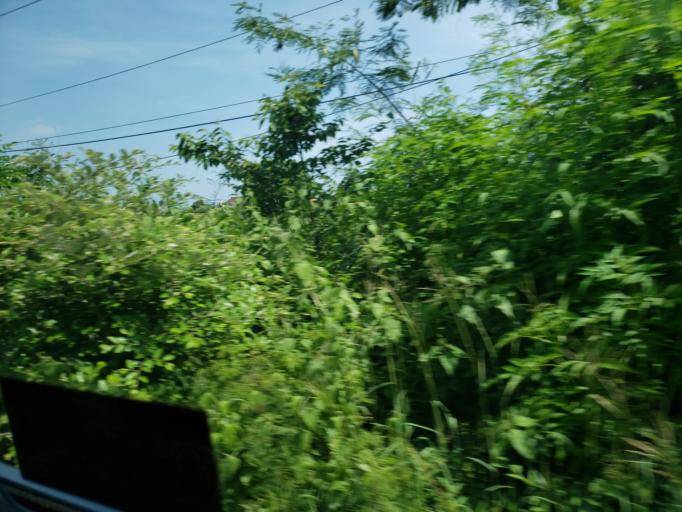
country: ID
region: Bali
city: Kangin
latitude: -8.8357
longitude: 115.1512
